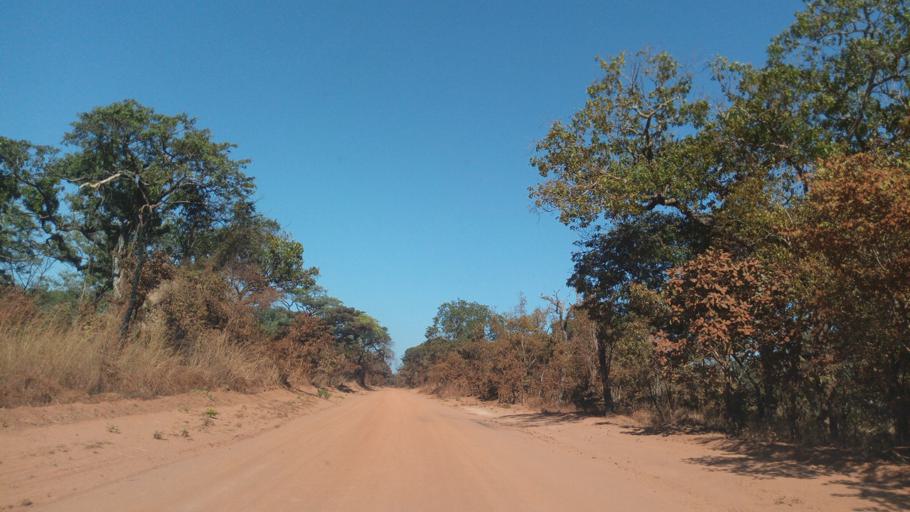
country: ZM
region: Luapula
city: Mwense
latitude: -10.7397
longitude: 28.3321
